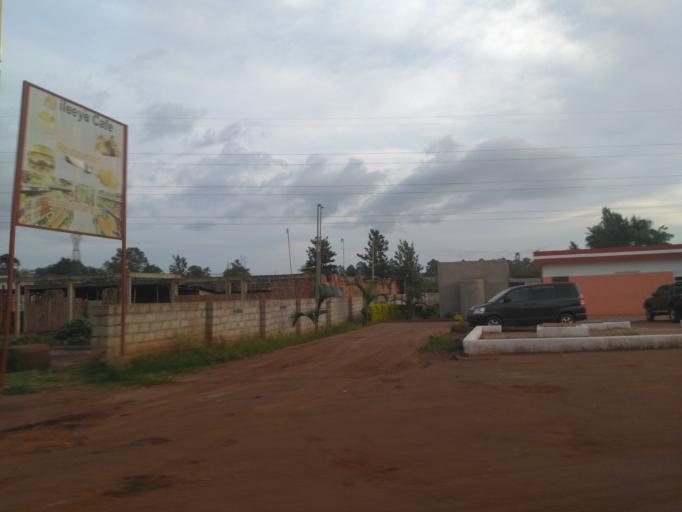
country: UG
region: Central Region
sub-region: Buikwe District
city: Njeru
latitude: 0.4382
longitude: 33.1739
